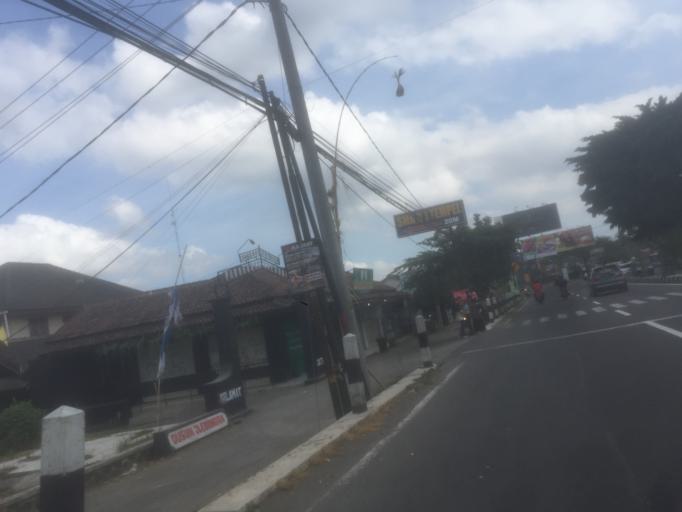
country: ID
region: Daerah Istimewa Yogyakarta
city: Sleman
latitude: -7.6586
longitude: 110.3268
